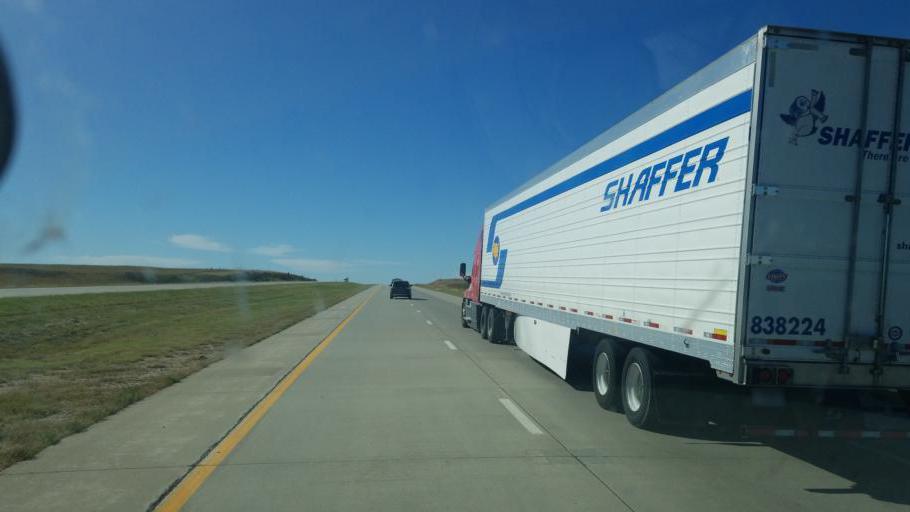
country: US
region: Kansas
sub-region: Riley County
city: Ogden
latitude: 39.0660
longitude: -96.6811
